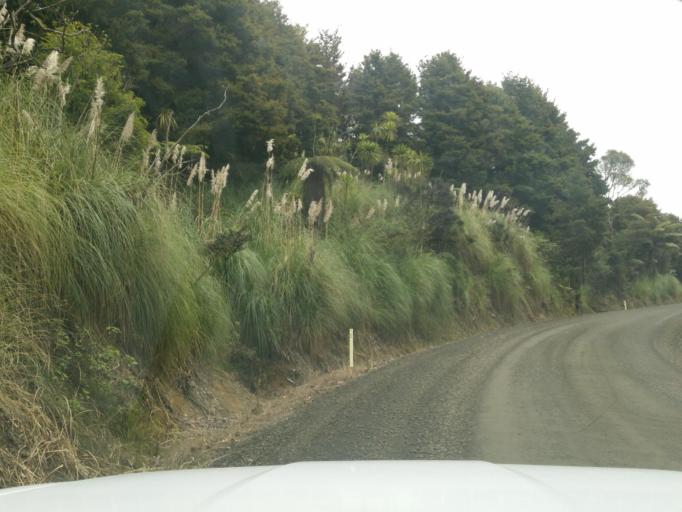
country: NZ
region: Northland
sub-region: Kaipara District
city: Dargaville
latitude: -35.7887
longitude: 173.9683
